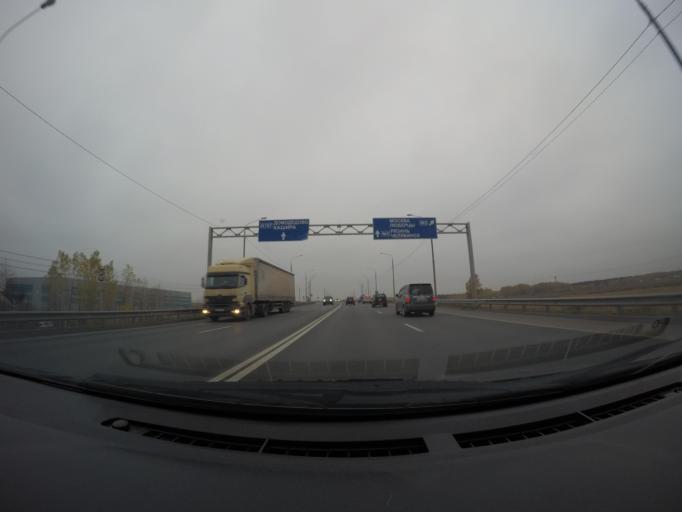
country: RU
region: Moskovskaya
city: Bronnitsy
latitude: 55.4140
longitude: 38.2417
